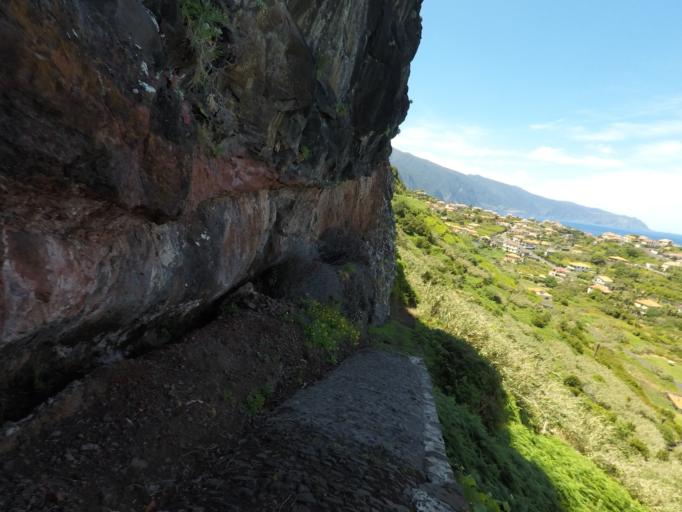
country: PT
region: Madeira
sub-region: Sao Vicente
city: Sao Vicente
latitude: 32.8257
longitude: -16.9833
